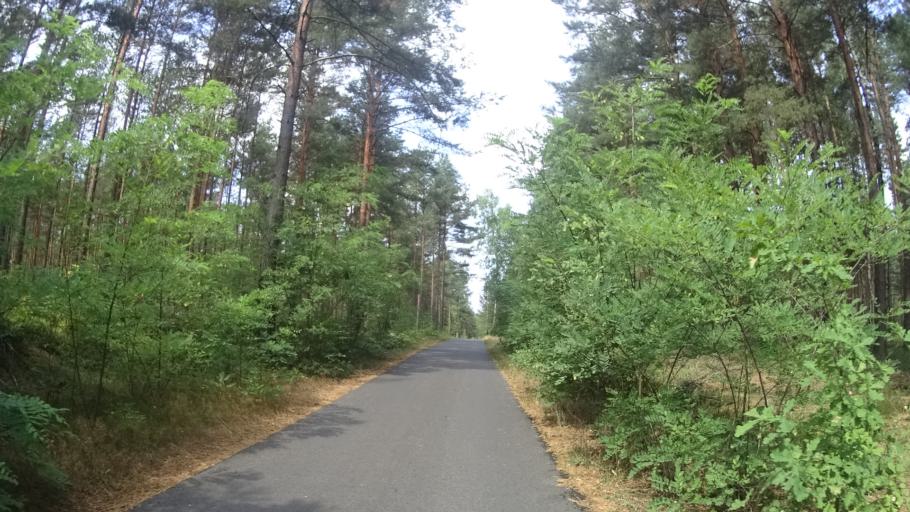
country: DE
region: Brandenburg
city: Tschernitz
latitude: 51.5940
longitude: 14.5972
